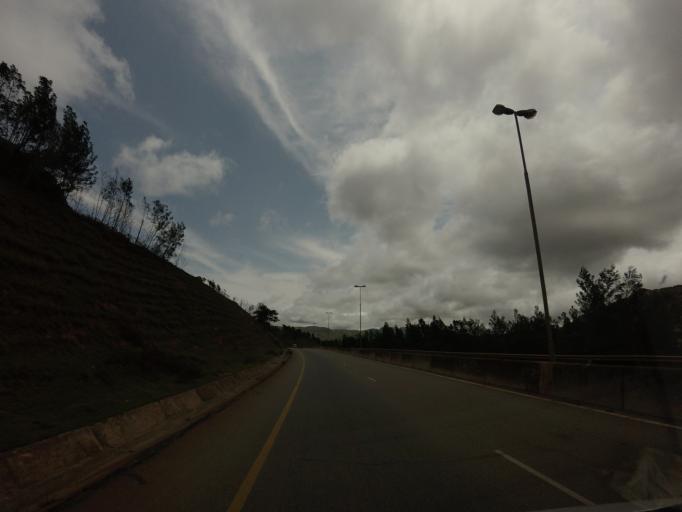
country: SZ
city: Darkton
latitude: -26.2591
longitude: 31.0692
